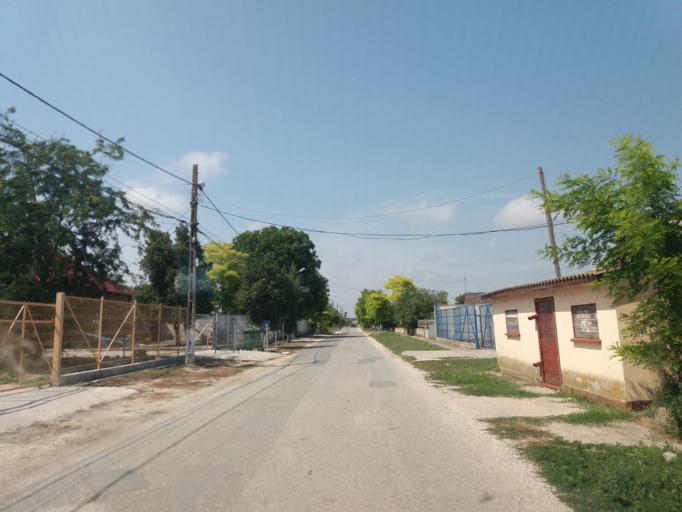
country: RO
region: Constanta
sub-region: Comuna Sacele
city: Sacele
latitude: 44.4501
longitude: 28.7368
